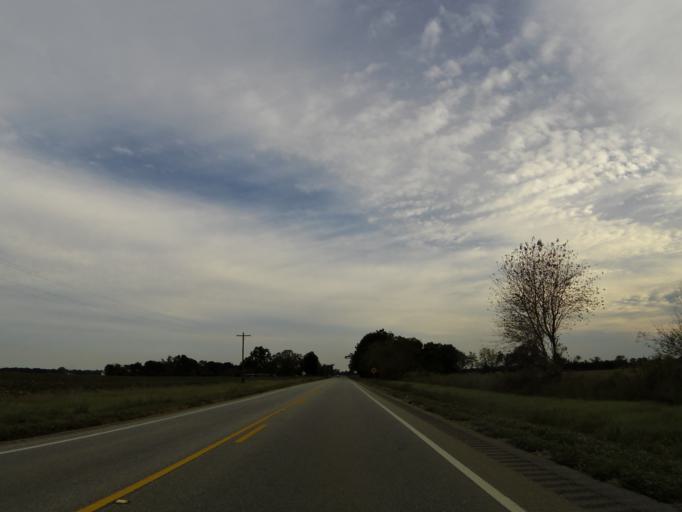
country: US
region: Alabama
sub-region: Monroe County
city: Frisco City
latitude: 31.3945
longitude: -87.4288
